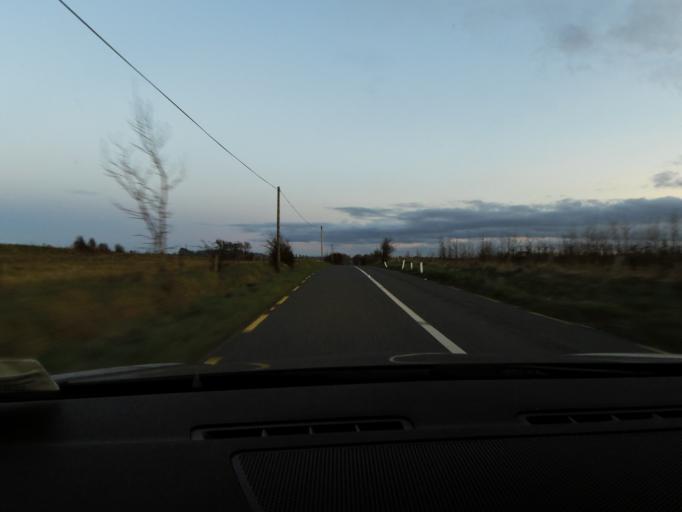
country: IE
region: Connaught
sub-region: Roscommon
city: Boyle
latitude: 53.8573
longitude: -8.2319
